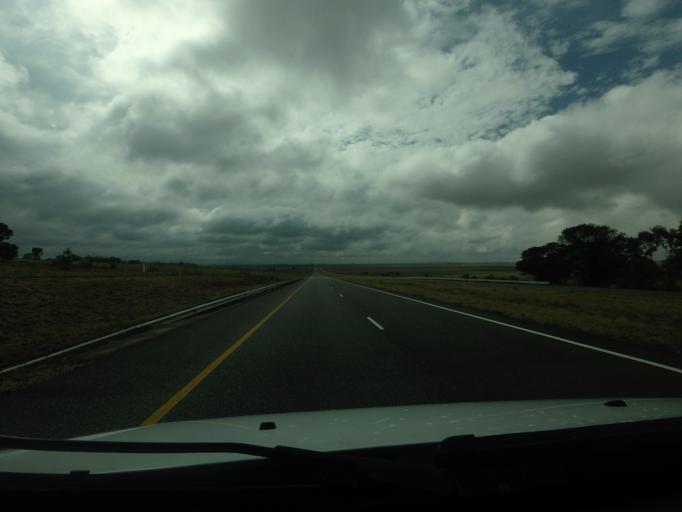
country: ZA
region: Gauteng
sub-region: City of Tshwane Metropolitan Municipality
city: Bronkhorstspruit
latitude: -25.8013
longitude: 28.6716
